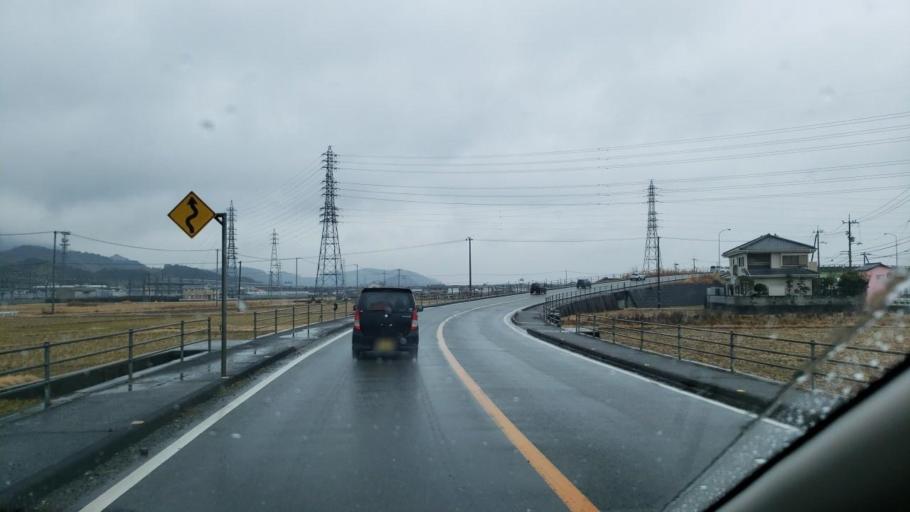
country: JP
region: Tokushima
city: Narutocho-mitsuishi
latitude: 34.1615
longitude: 134.5521
